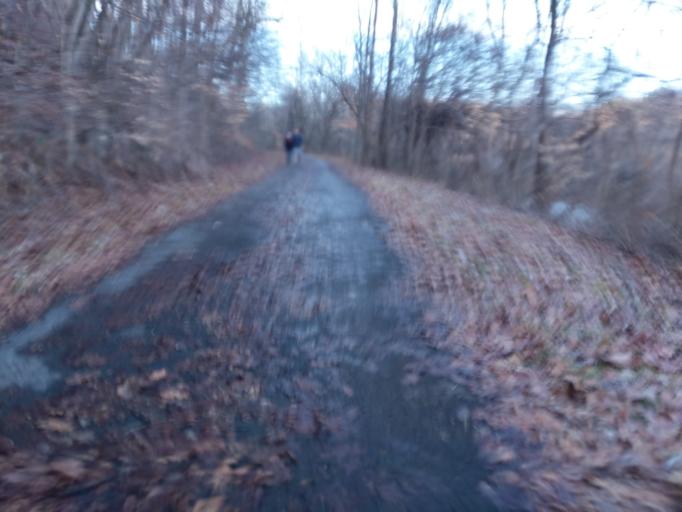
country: US
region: Ohio
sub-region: Athens County
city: Athens
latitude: 39.3496
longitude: -82.1021
